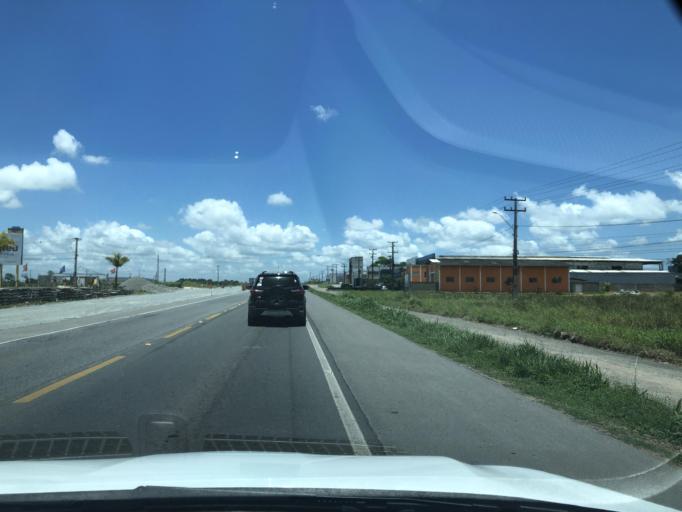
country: BR
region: Santa Catarina
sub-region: Joinville
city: Joinville
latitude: -26.3844
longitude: -48.7279
